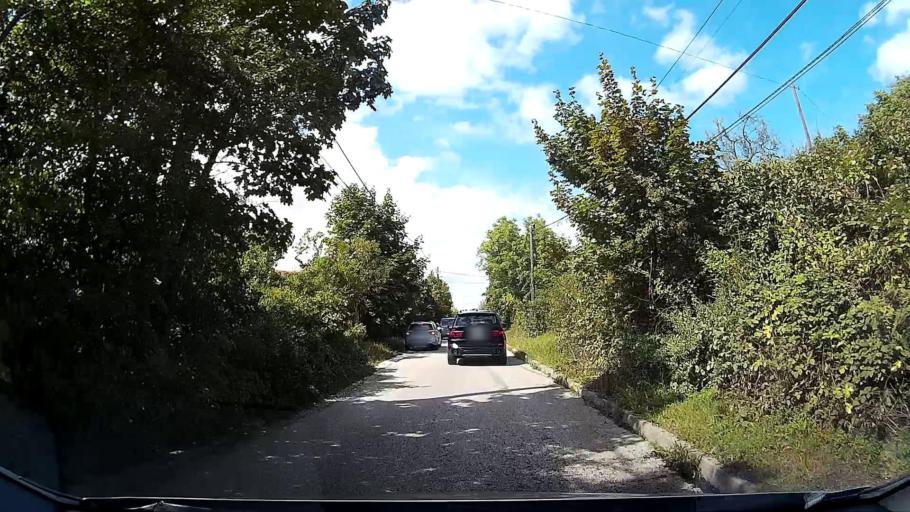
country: HU
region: Pest
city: Szentendre
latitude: 47.6870
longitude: 19.0737
